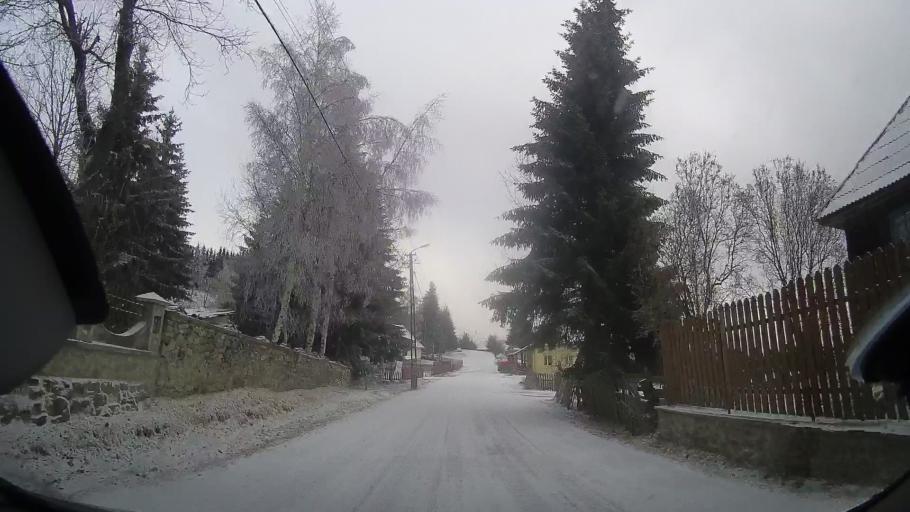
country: RO
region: Cluj
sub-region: Comuna Marisel
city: Marisel
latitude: 46.6617
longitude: 23.1288
